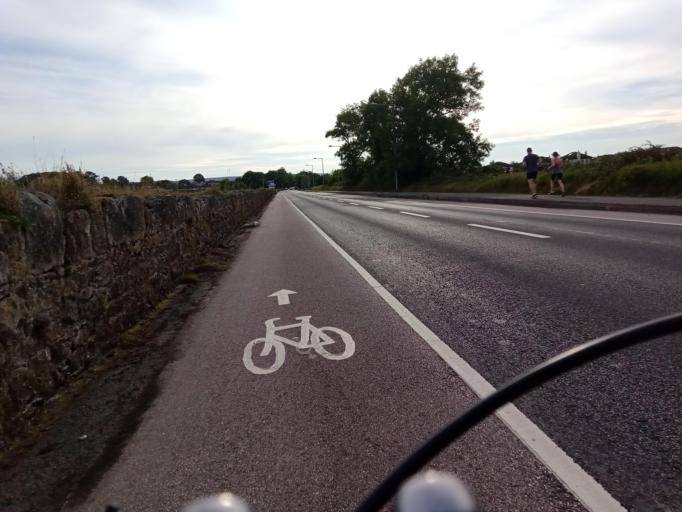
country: IE
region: Munster
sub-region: Waterford
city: Dungarvan
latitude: 52.0975
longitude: -7.5945
